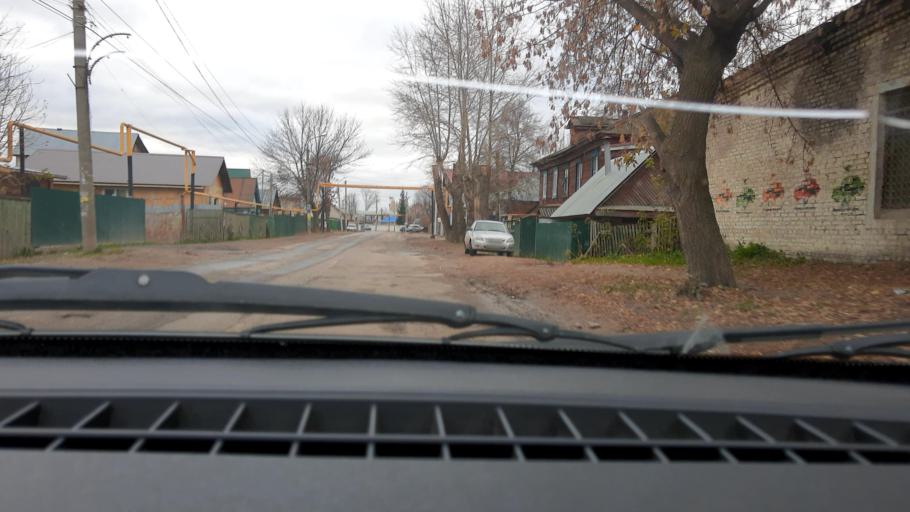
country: RU
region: Bashkortostan
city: Mikhaylovka
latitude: 54.7371
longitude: 55.8976
